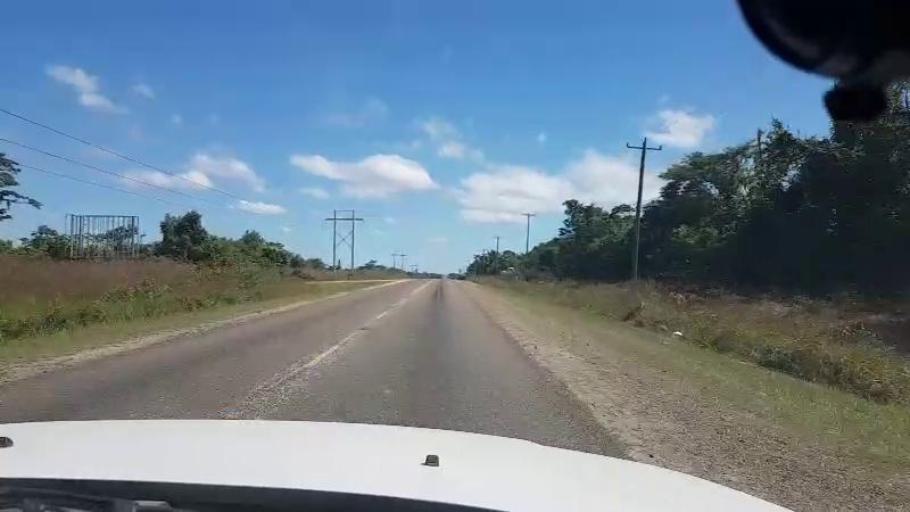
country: BZ
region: Cayo
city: Belmopan
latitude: 17.2768
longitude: -88.7322
